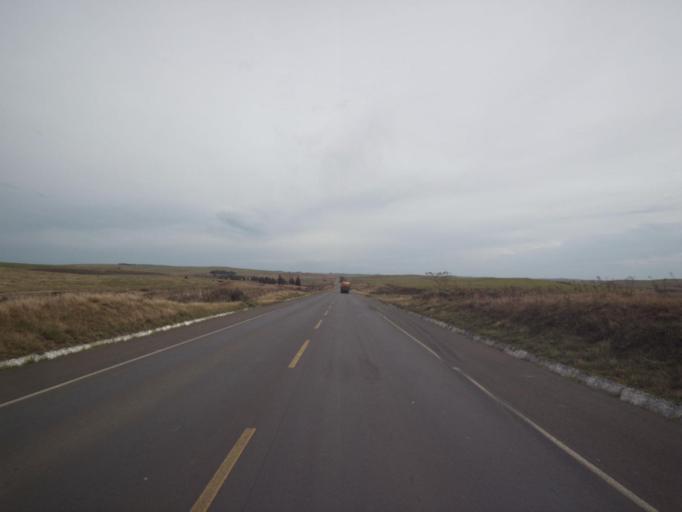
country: BR
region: Parana
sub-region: Palmas
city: Palmas
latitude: -26.7212
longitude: -51.6244
